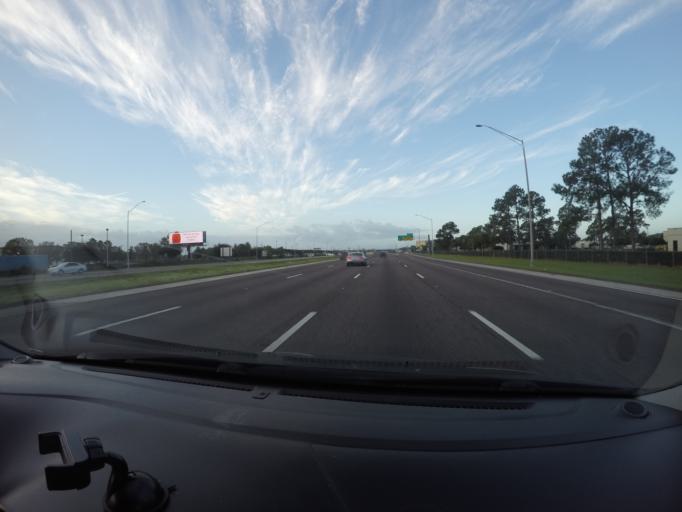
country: US
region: Florida
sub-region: Orange County
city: Oak Ridge
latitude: 28.4992
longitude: -81.4285
